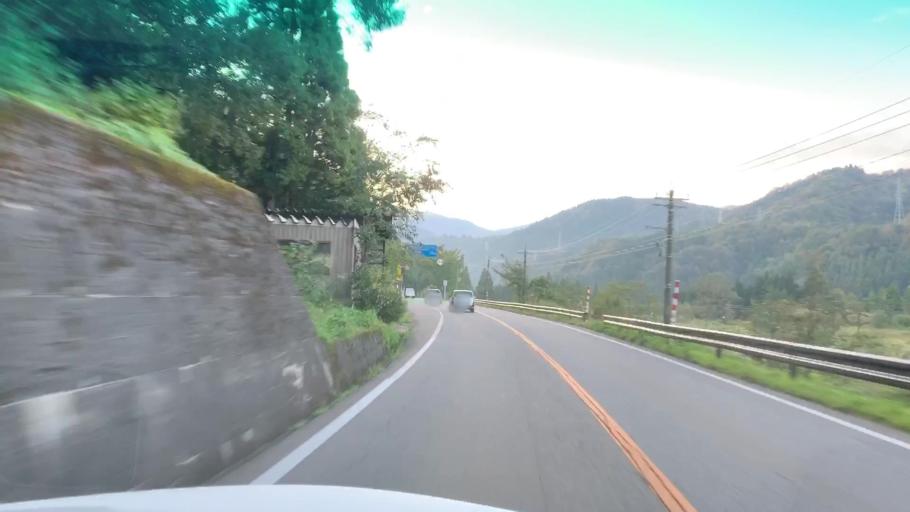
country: JP
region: Toyama
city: Kamiichi
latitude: 36.5807
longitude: 137.3378
